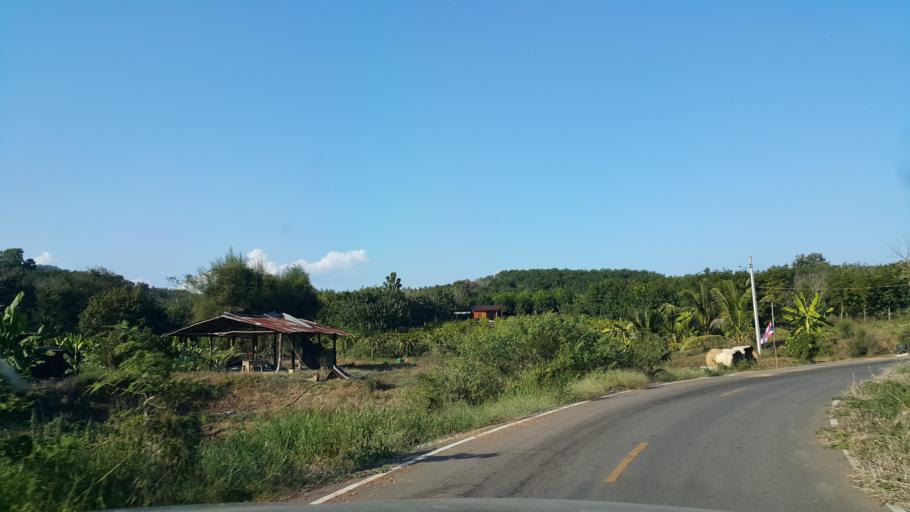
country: TH
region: Sukhothai
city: Thung Saliam
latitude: 17.4005
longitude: 99.5096
